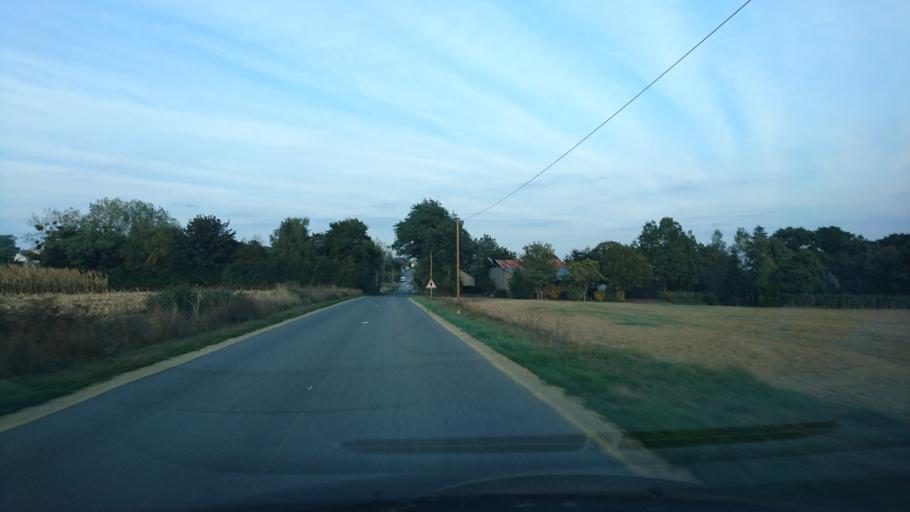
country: FR
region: Brittany
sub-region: Departement d'Ille-et-Vilaine
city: Maure-de-Bretagne
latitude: 47.8497
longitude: -2.0124
